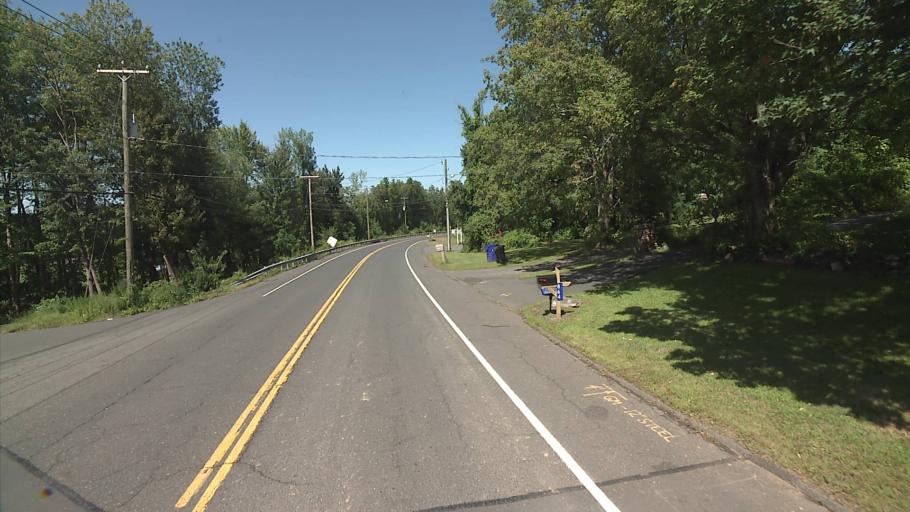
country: US
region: Connecticut
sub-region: Hartford County
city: Windsor Locks
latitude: 41.9562
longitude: -72.6278
